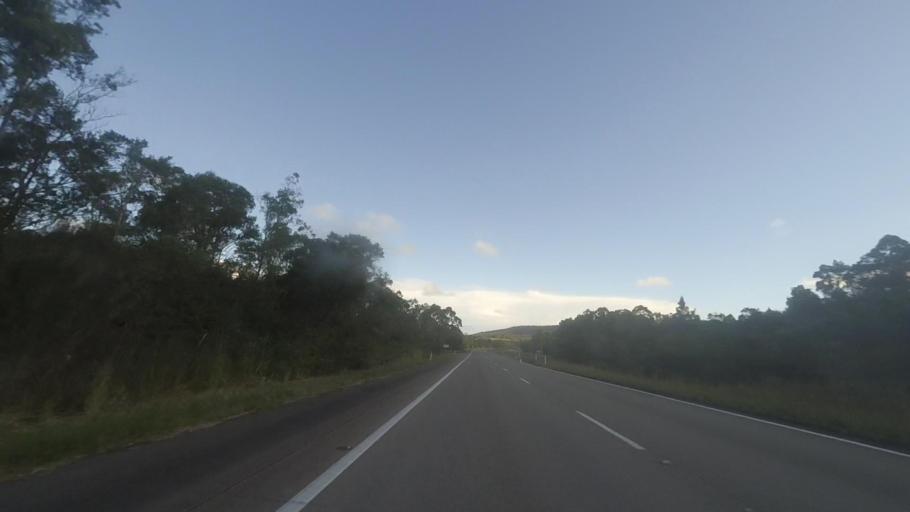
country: AU
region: New South Wales
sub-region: Great Lakes
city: Nabiac
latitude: -32.2590
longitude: 152.3261
